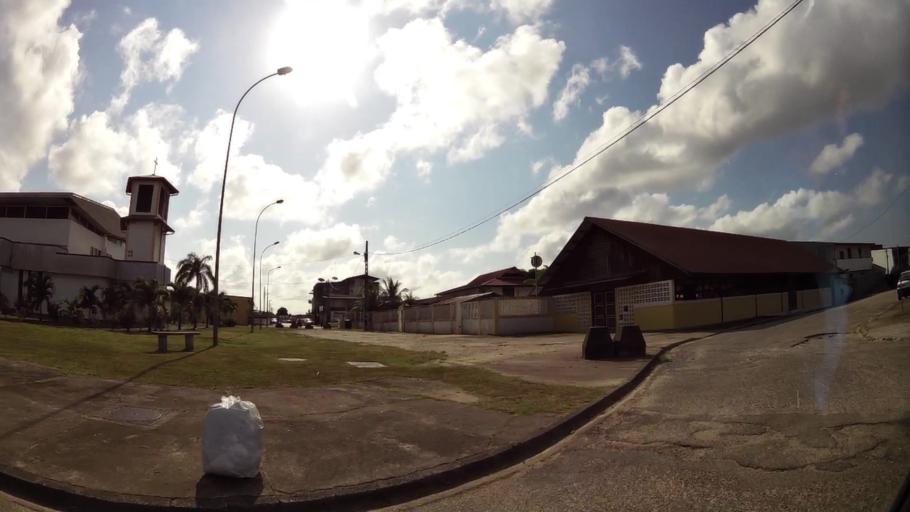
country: GF
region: Guyane
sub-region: Guyane
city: Cayenne
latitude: 4.9337
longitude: -52.3255
